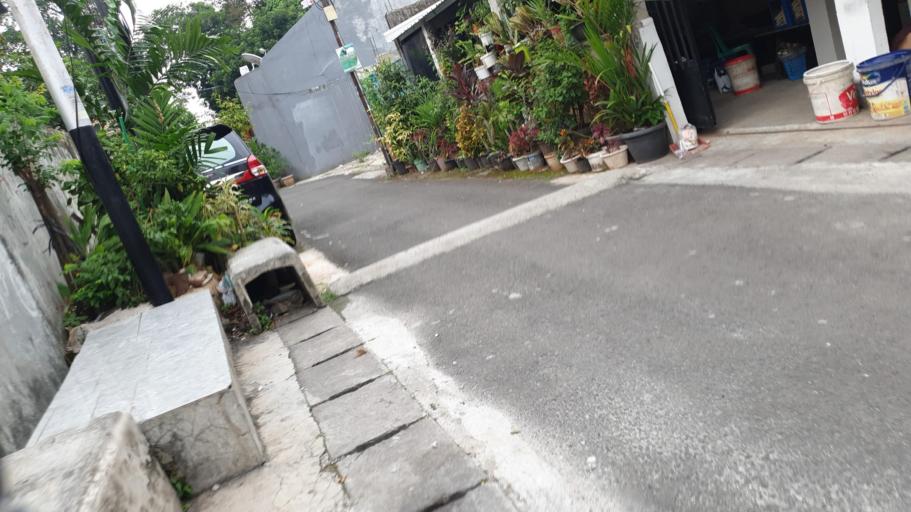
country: ID
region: Banten
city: South Tangerang
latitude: -6.2626
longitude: 106.7873
